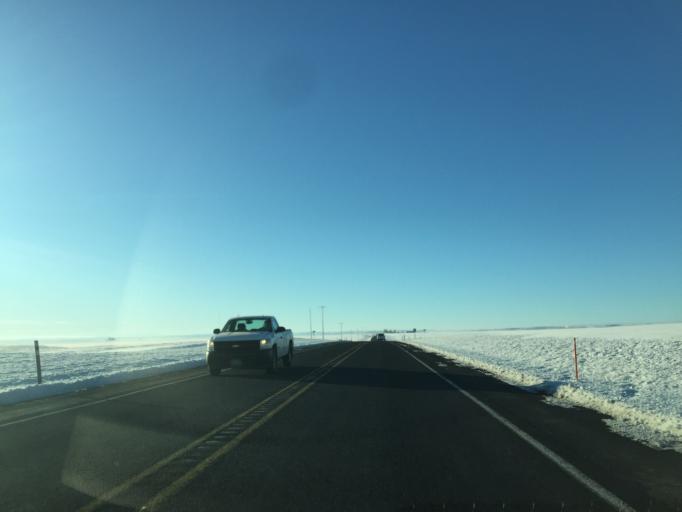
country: US
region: Washington
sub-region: Okanogan County
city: Coulee Dam
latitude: 47.6845
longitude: -118.9951
